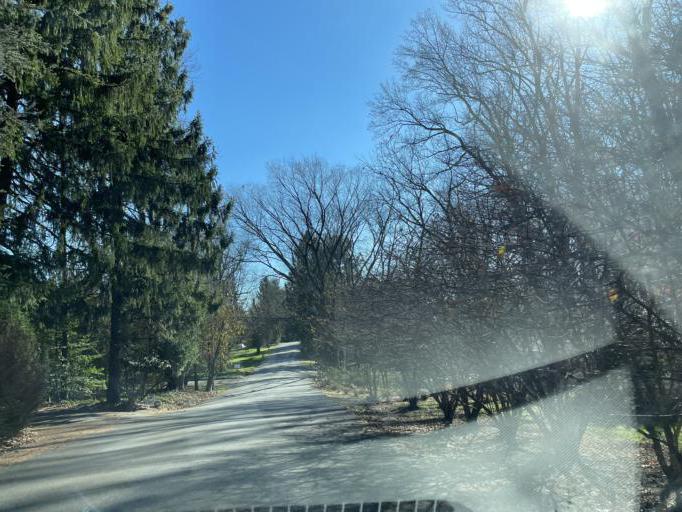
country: US
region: Maryland
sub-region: Baltimore County
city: Mays Chapel
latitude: 39.3965
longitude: -76.6574
